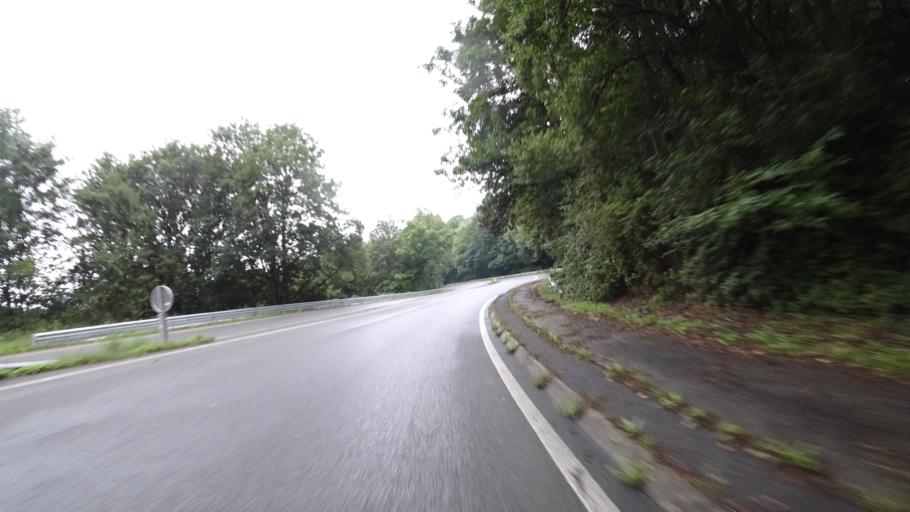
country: BE
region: Wallonia
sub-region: Province de Namur
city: Namur
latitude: 50.4912
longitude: 4.8177
